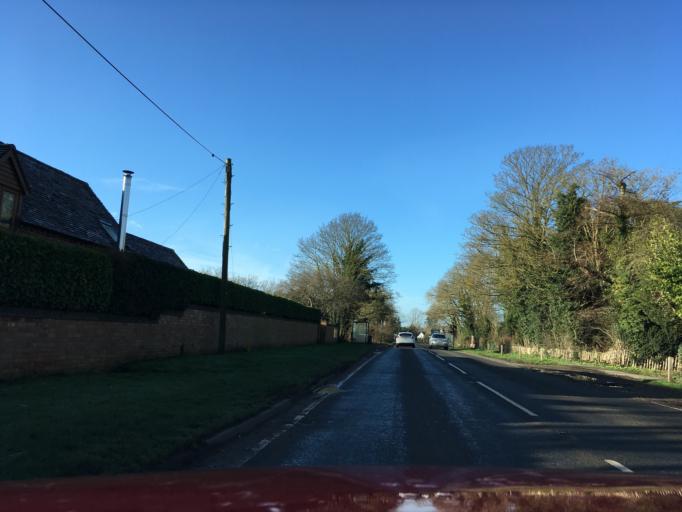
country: GB
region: England
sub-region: Warwickshire
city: Stratford-upon-Avon
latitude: 52.2031
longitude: -1.6628
